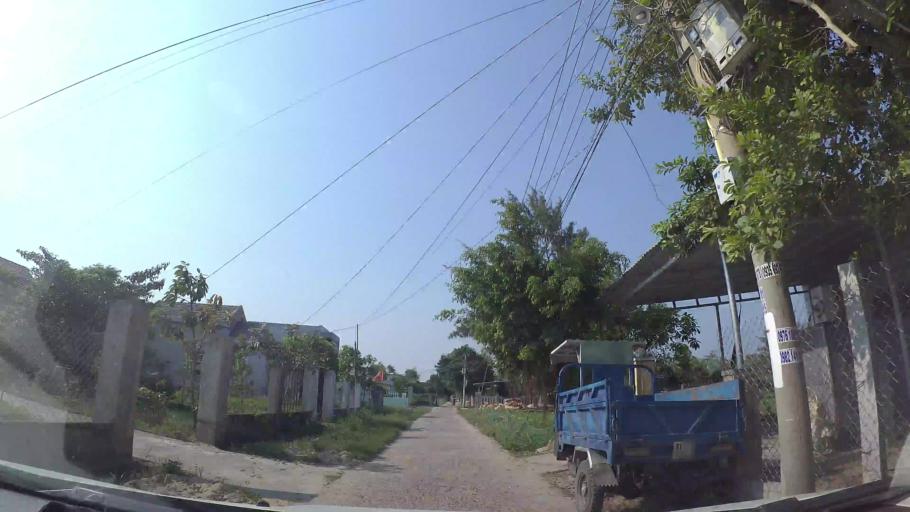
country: VN
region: Da Nang
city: Ngu Hanh Son
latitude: 15.9542
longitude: 108.2657
